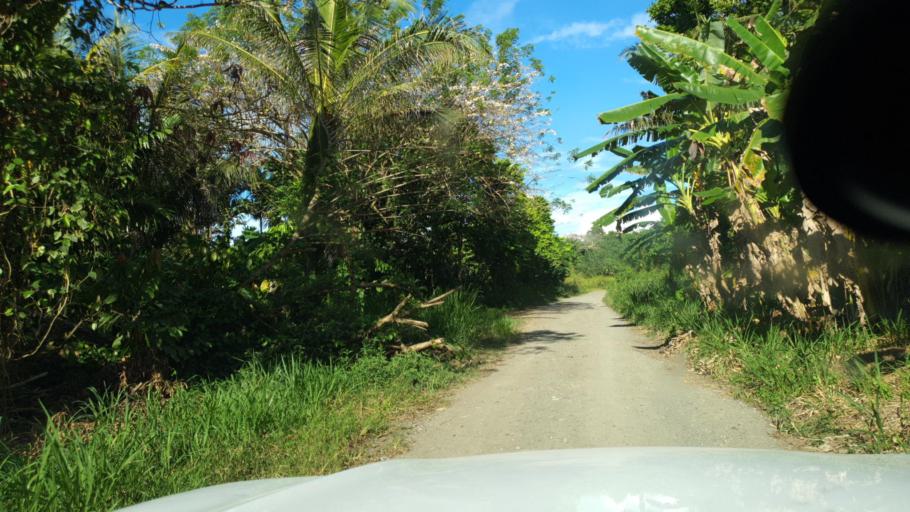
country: SB
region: Guadalcanal
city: Honiara
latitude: -9.4451
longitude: 160.1538
